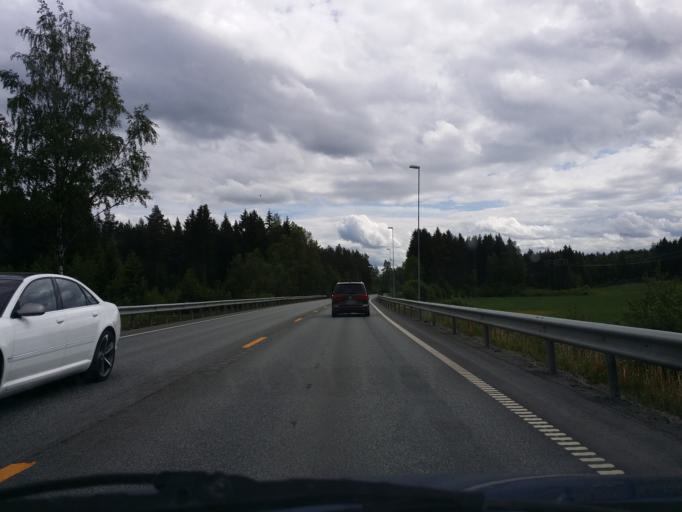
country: NO
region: Hedmark
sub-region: Stange
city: Stange
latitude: 60.7428
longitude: 11.2062
